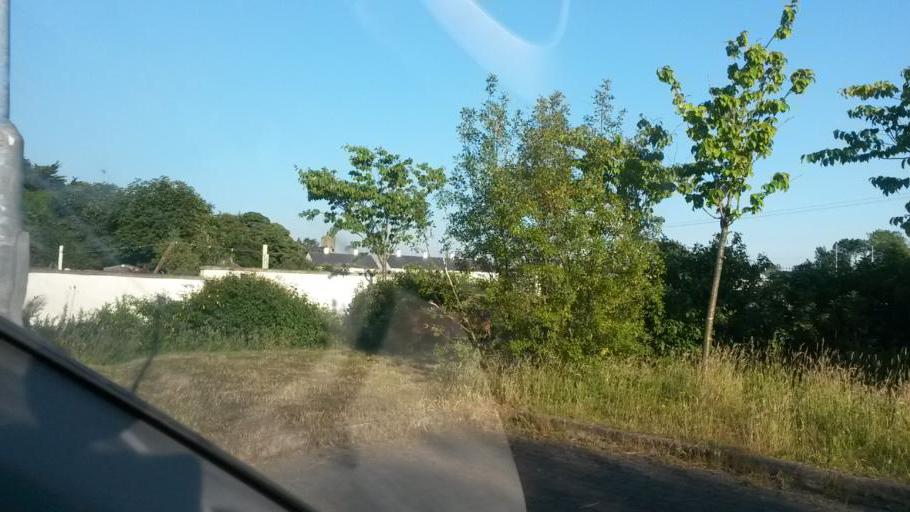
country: IE
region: Leinster
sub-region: An Mhi
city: Ashbourne
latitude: 53.5652
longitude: -6.3867
